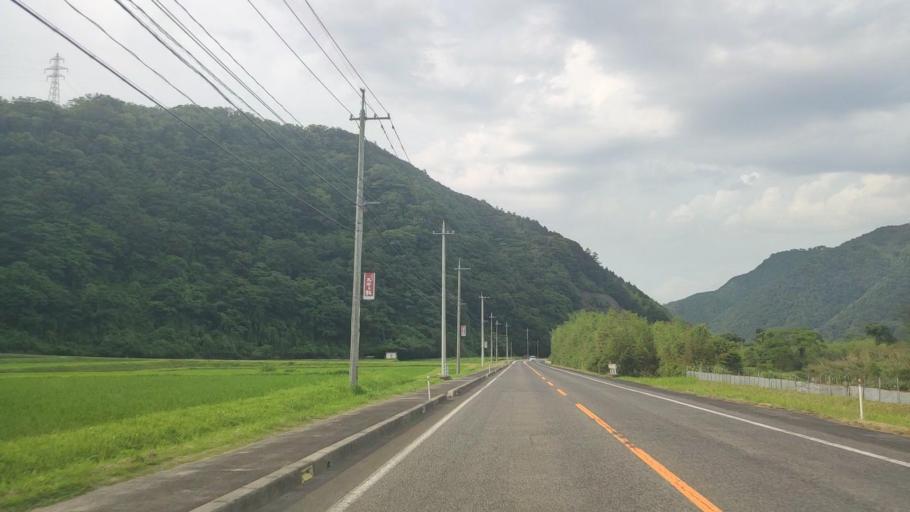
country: JP
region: Tottori
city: Kurayoshi
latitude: 35.3612
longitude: 133.8462
